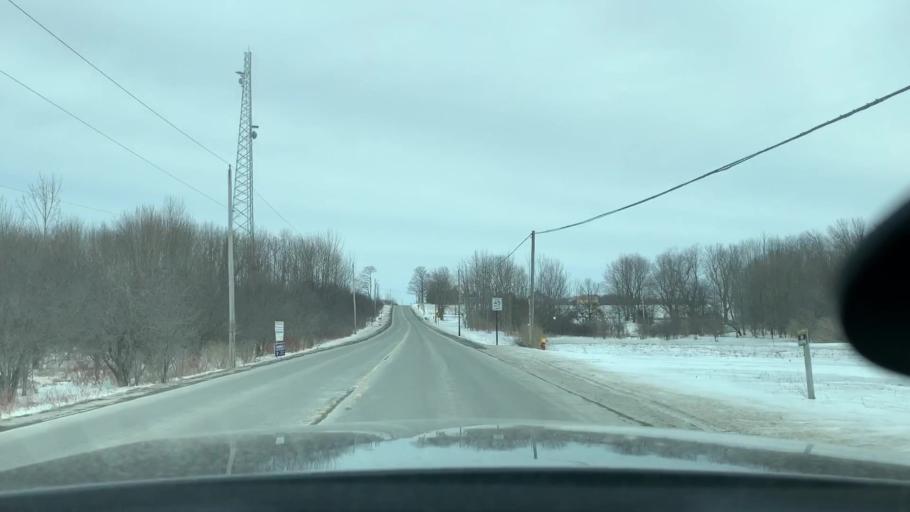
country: US
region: New York
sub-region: Oneida County
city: Washington Mills
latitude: 43.0488
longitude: -75.2314
